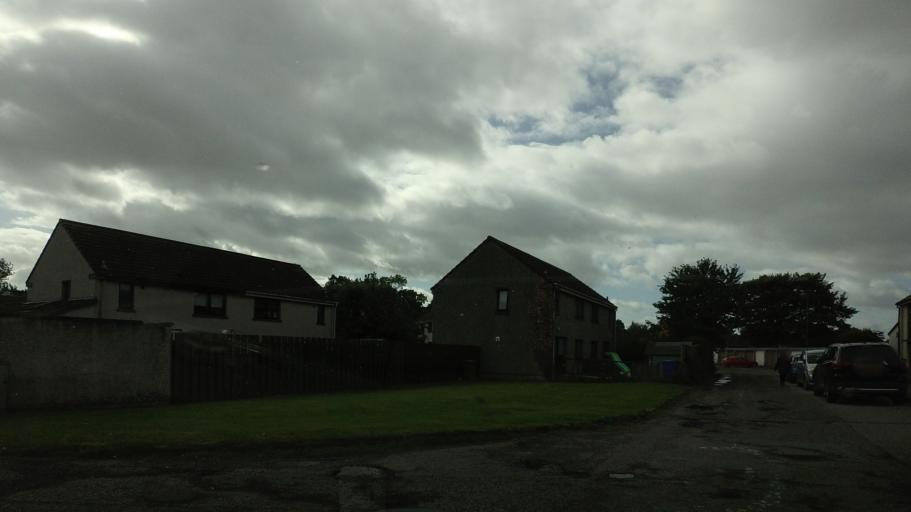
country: GB
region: Scotland
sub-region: Highland
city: Alness
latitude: 57.6942
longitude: -4.2713
